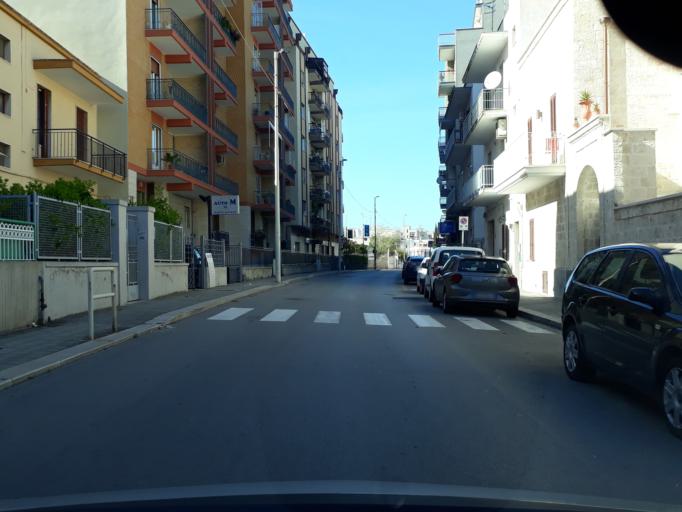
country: IT
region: Apulia
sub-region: Provincia di Bari
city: Monopoli
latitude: 40.9471
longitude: 17.2996
